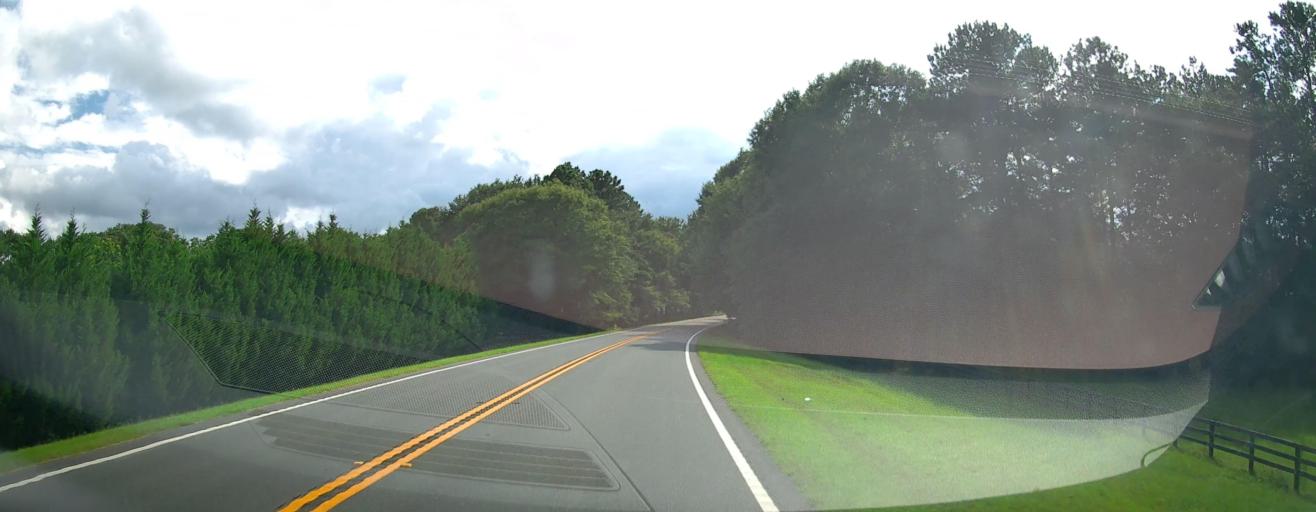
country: US
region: Georgia
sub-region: Meriwether County
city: Manchester
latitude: 32.9887
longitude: -84.5789
